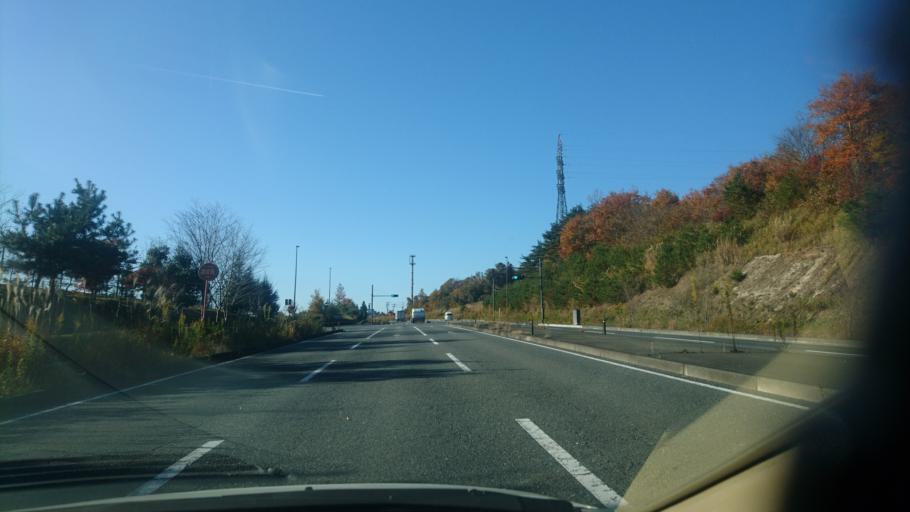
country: JP
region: Miyagi
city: Tomiya
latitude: 38.4736
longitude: 140.9017
